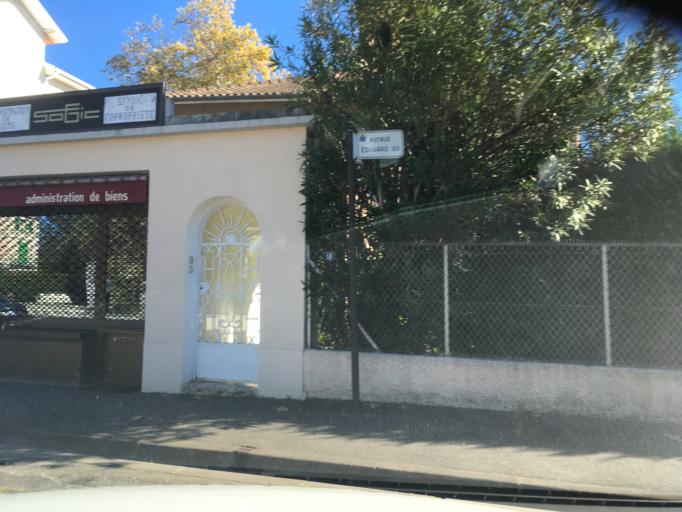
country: FR
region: Aquitaine
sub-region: Departement des Pyrenees-Atlantiques
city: Pau
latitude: 43.2973
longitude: -0.3584
